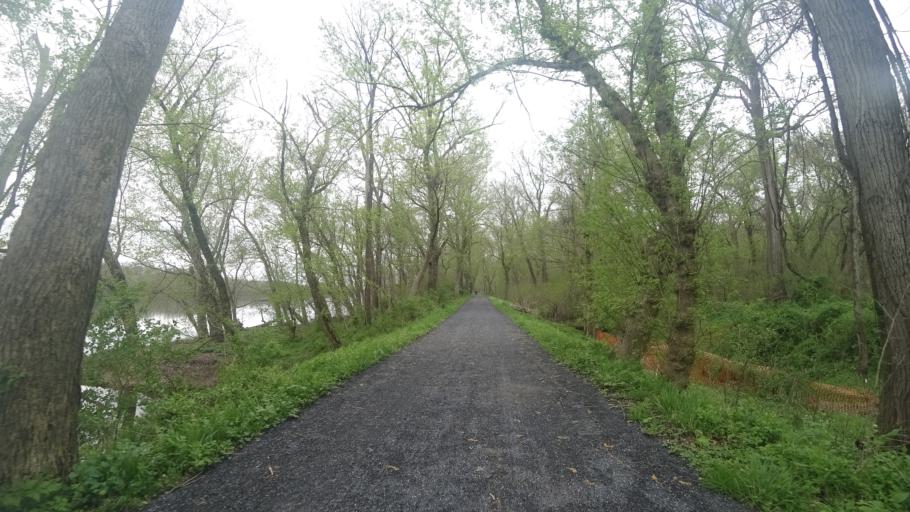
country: US
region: Virginia
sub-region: Loudoun County
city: Countryside
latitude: 39.0724
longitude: -77.4125
